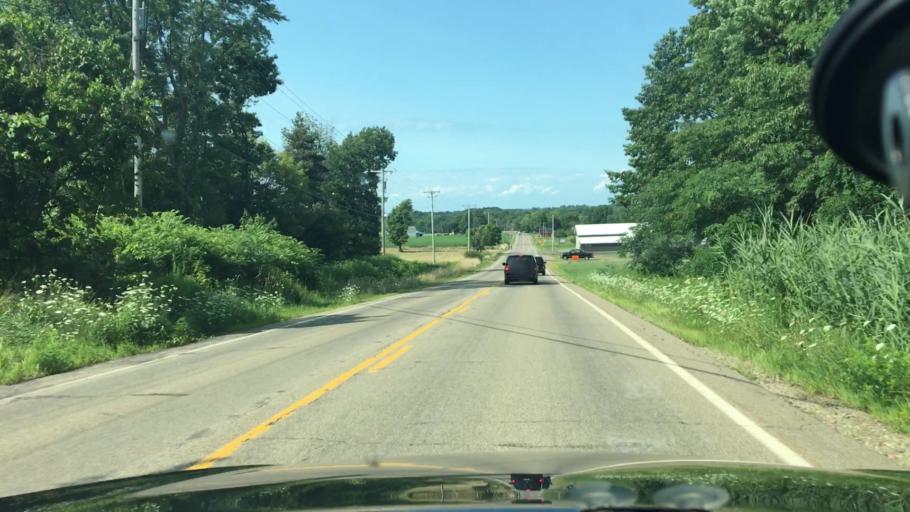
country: US
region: New York
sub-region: Chautauqua County
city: Fredonia
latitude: 42.4133
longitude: -79.3129
